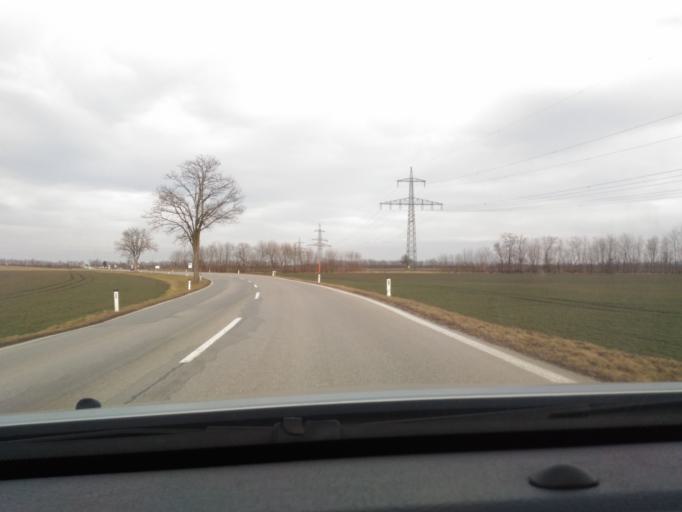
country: AT
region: Lower Austria
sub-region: Politischer Bezirk Mistelbach
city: Grossharras
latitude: 48.7050
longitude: 16.2781
